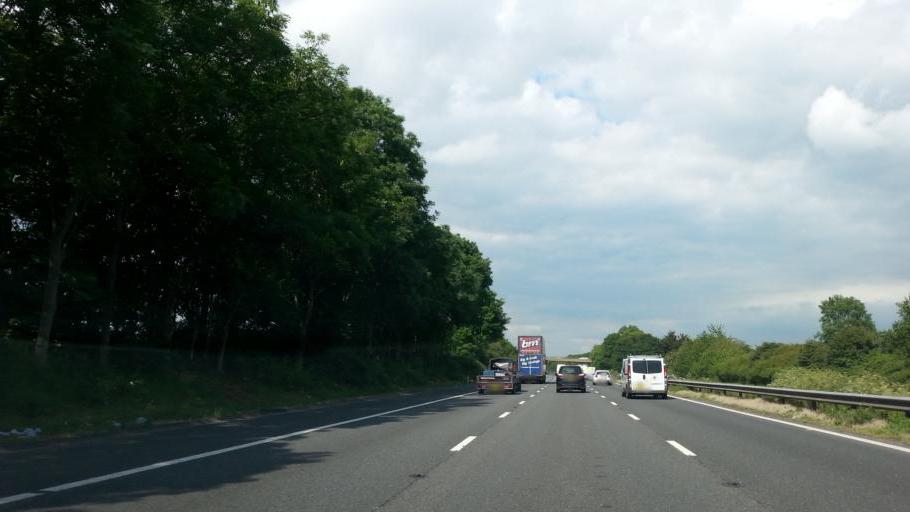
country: GB
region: England
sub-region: Gloucestershire
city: Uckington
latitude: 51.9354
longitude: -2.1327
